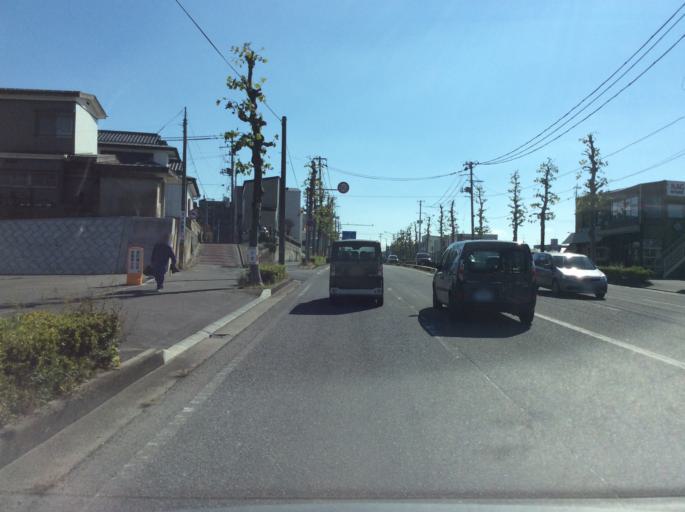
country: JP
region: Fukushima
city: Koriyama
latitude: 37.3954
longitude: 140.3628
